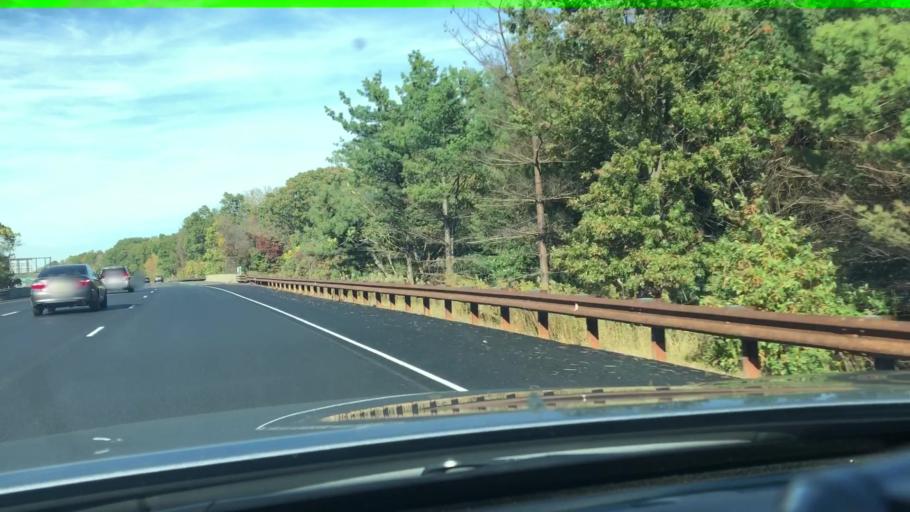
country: US
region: New Jersey
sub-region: Bergen County
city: Paramus
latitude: 40.9476
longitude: -74.0664
